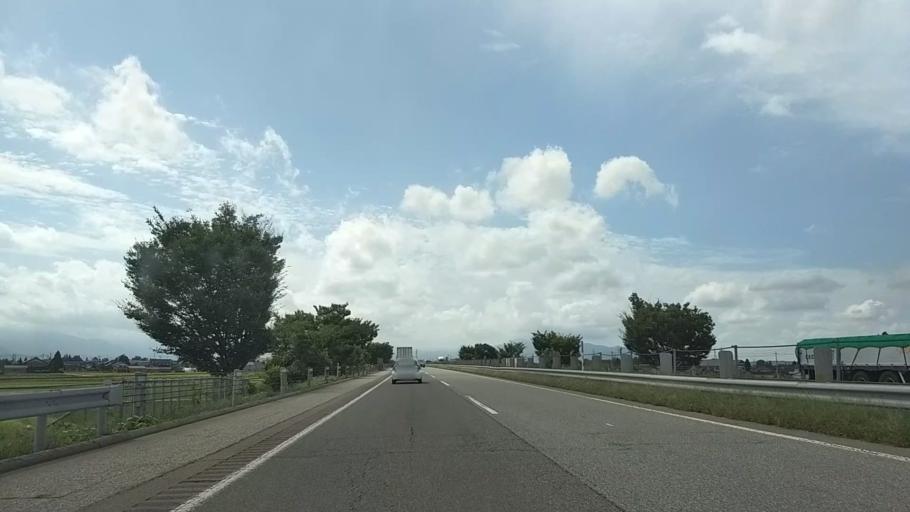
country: JP
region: Toyama
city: Nanto-shi
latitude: 36.6430
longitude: 136.9770
